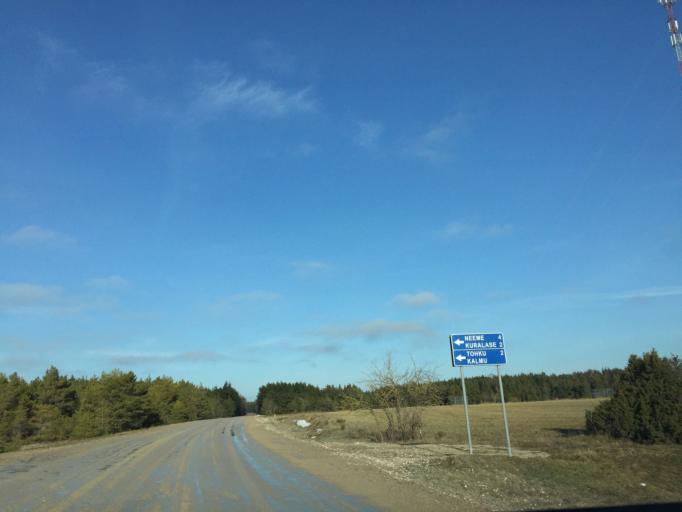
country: EE
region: Saare
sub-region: Kuressaare linn
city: Kuressaare
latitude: 58.4681
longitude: 22.0012
